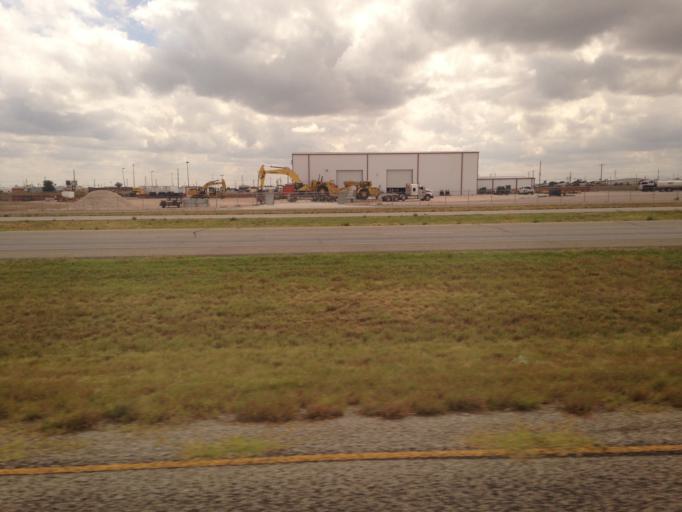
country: US
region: Texas
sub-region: Lubbock County
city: Lubbock
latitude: 33.5319
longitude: -101.8073
